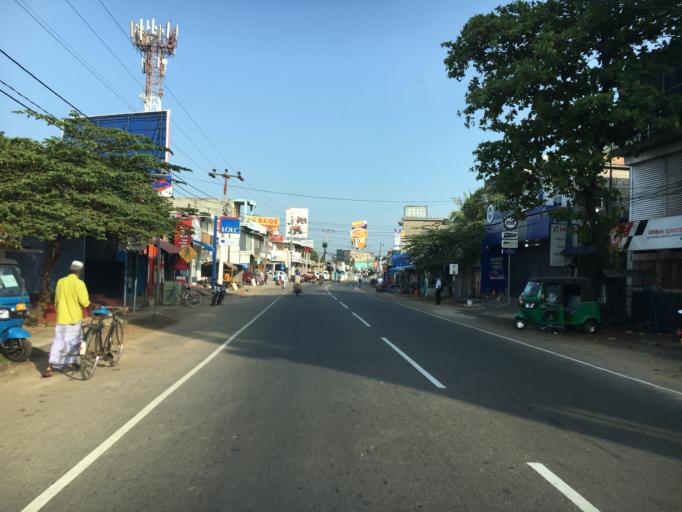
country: LK
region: Eastern Province
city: Eravur Town
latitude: 7.9141
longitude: 81.5235
